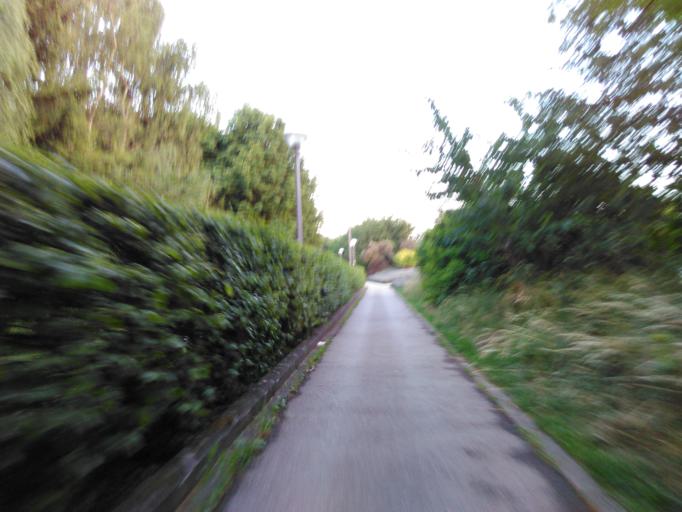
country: LU
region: Luxembourg
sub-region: Canton d'Esch-sur-Alzette
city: Esch-sur-Alzette
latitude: 49.5080
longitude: 5.9786
